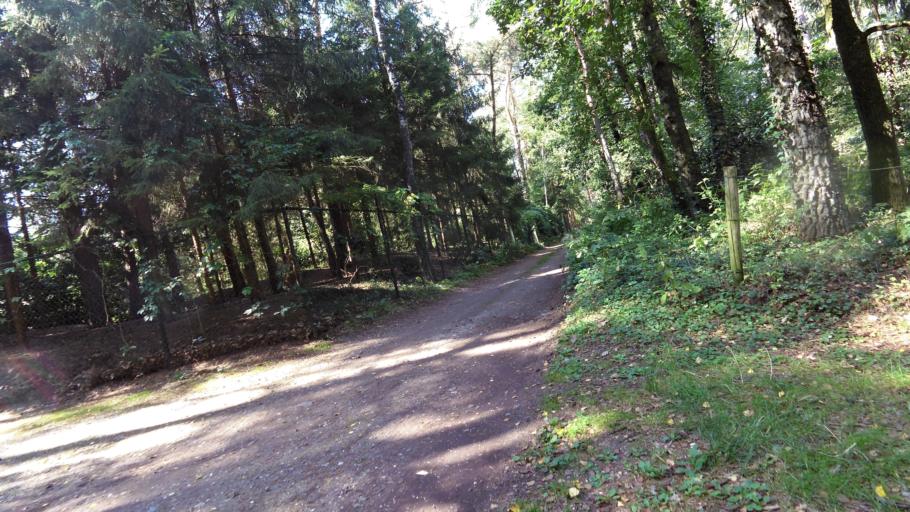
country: NL
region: Gelderland
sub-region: Gemeente Renkum
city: Renkum
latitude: 52.0081
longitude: 5.7309
